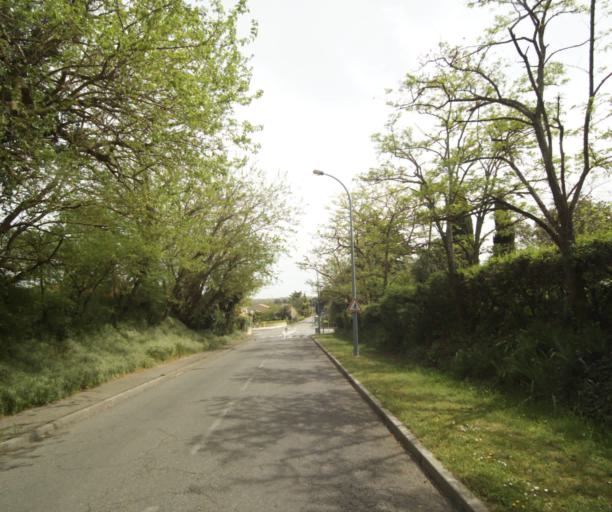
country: FR
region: Midi-Pyrenees
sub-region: Departement de la Haute-Garonne
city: Auzeville-Tolosane
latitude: 43.5279
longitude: 1.4928
